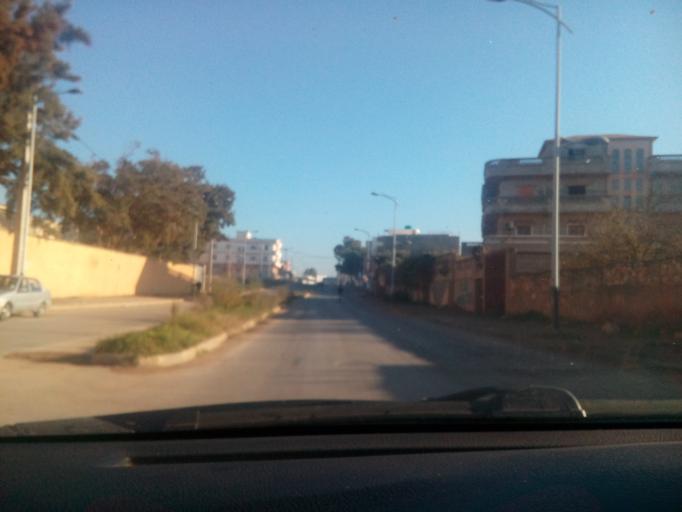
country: DZ
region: Oran
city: Bir el Djir
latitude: 35.7574
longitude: -0.5379
